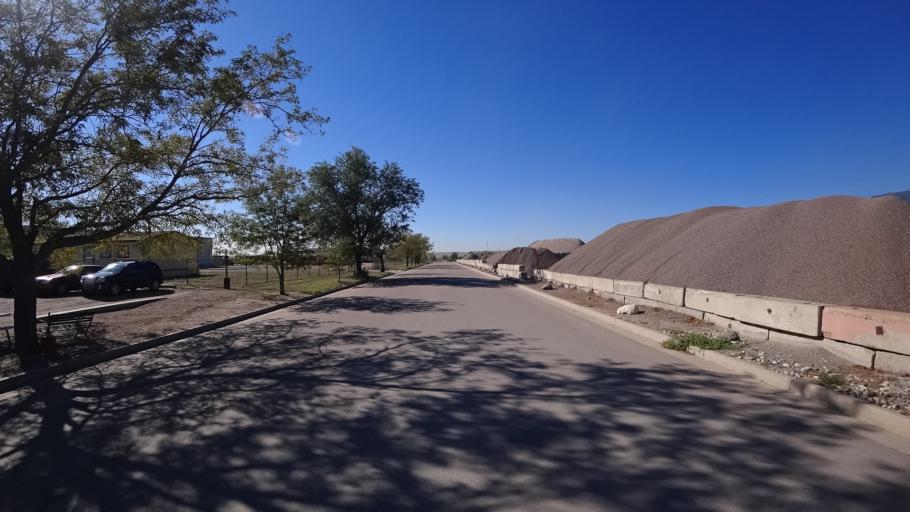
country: US
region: Colorado
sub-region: El Paso County
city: Stratmoor
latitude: 38.7814
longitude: -104.7639
